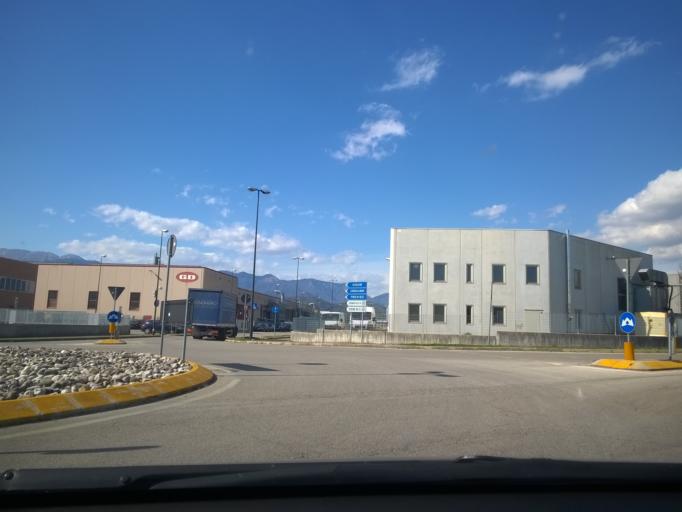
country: IT
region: Veneto
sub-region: Provincia di Treviso
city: Falze di Piave
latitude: 45.8762
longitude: 12.1678
